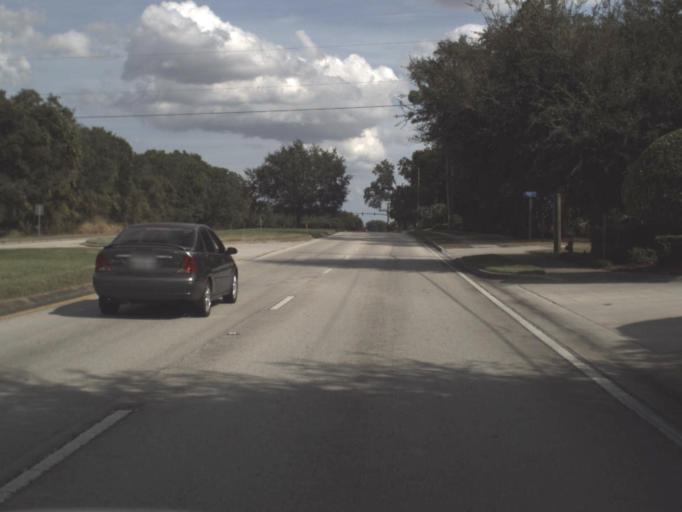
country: US
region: Florida
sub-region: Seminole County
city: Lake Mary
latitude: 28.7562
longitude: -81.3148
